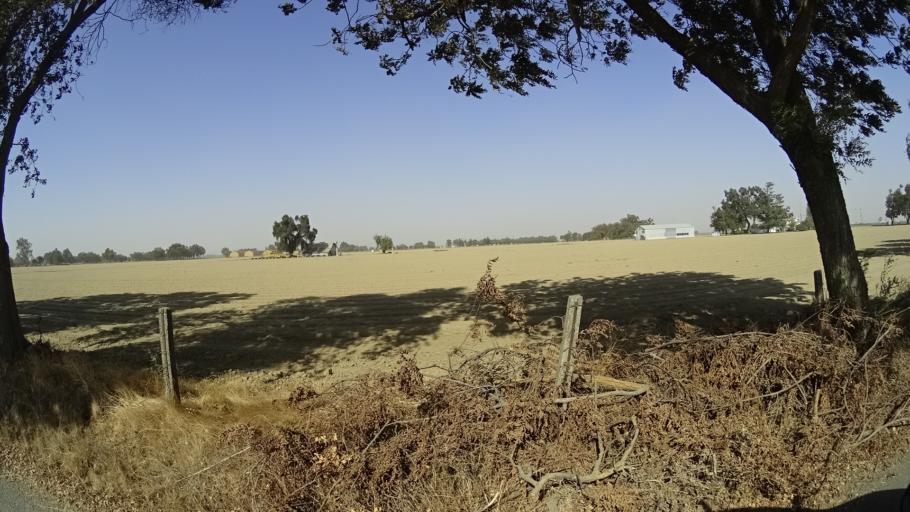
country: US
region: California
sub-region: Yolo County
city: Woodland
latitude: 38.7351
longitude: -121.7788
